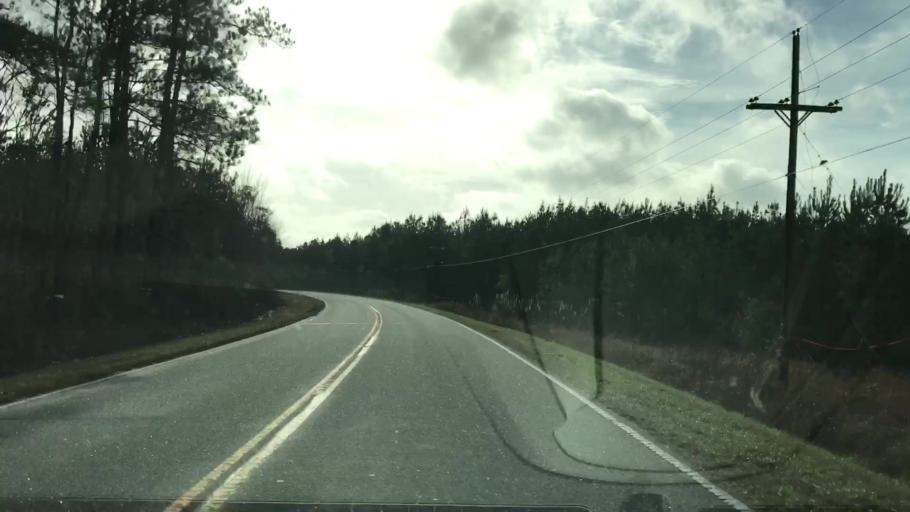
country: US
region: South Carolina
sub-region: Williamsburg County
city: Andrews
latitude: 33.4186
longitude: -79.6022
